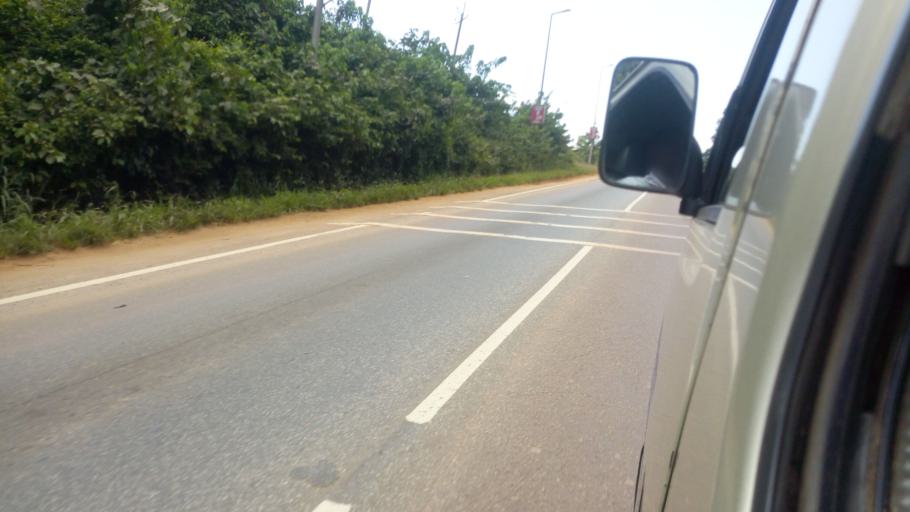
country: GH
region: Central
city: Cape Coast
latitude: 5.1109
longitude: -1.2780
